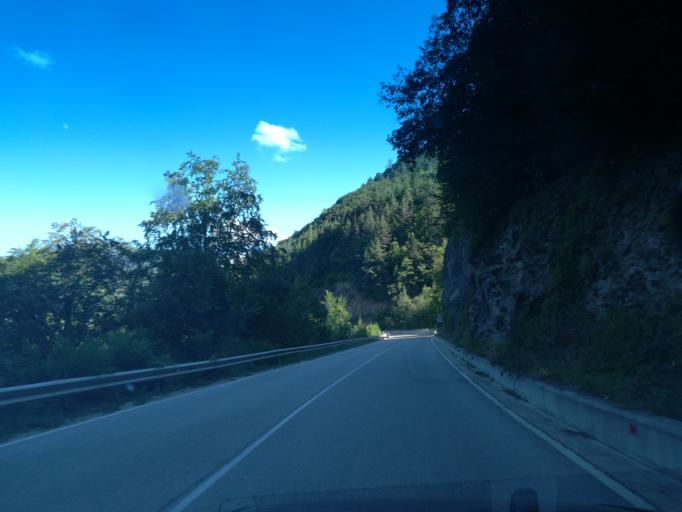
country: BG
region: Smolyan
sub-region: Obshtina Chepelare
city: Chepelare
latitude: 41.8146
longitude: 24.7029
